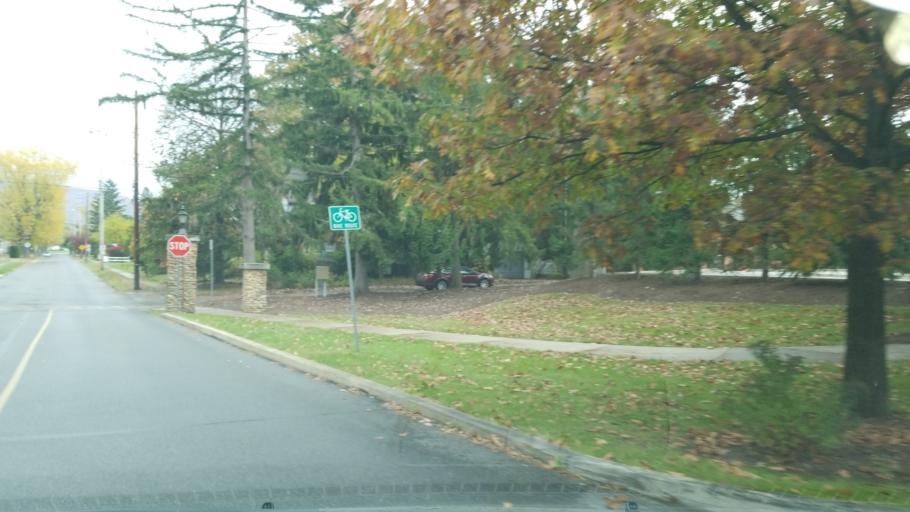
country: US
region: Pennsylvania
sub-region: Blair County
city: Altoona
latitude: 40.5383
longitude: -78.4051
